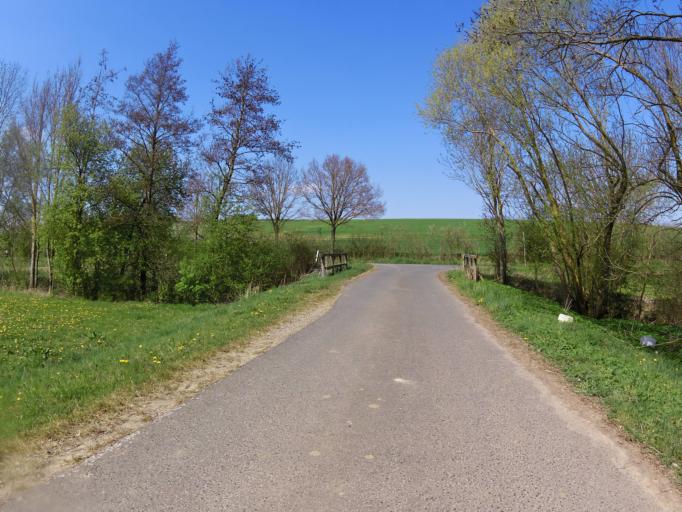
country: DE
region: Bavaria
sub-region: Regierungsbezirk Unterfranken
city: Dettelbach
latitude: 49.8213
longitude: 10.1368
